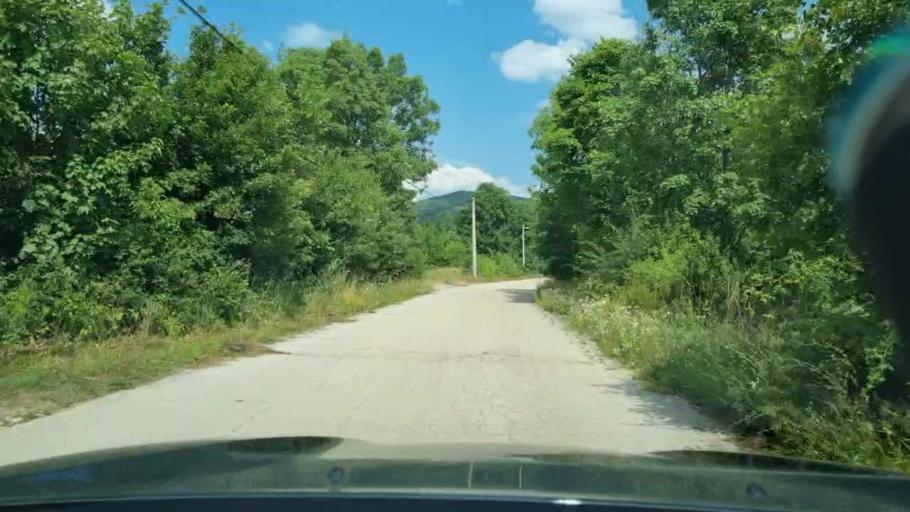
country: BA
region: Federation of Bosnia and Herzegovina
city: Bosansko Grahovo
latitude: 44.2949
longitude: 16.2910
